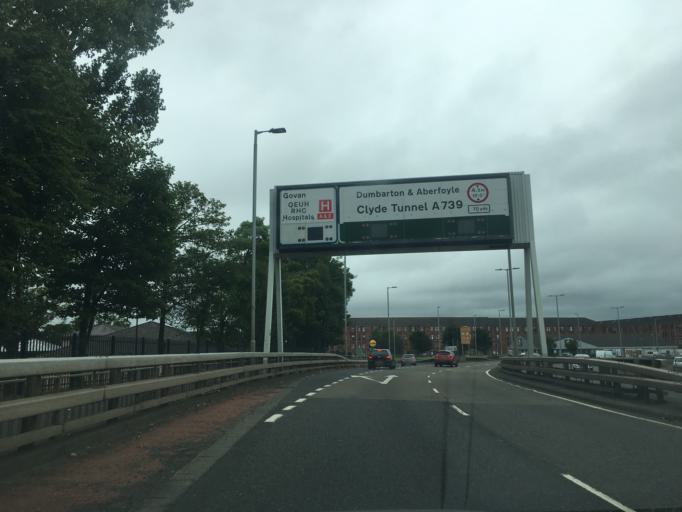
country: GB
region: Scotland
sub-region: East Dunbartonshire
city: Bearsden
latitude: 55.8621
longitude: -4.3365
